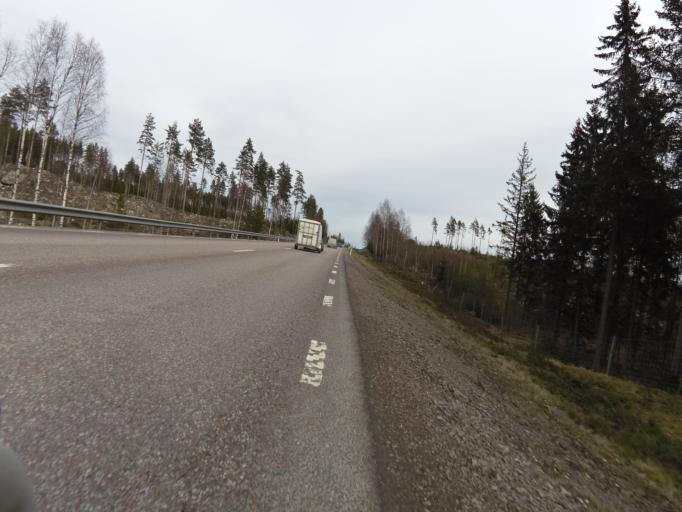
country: SE
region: Gaevleborg
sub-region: Hofors Kommun
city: Hofors
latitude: 60.5426
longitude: 16.2042
